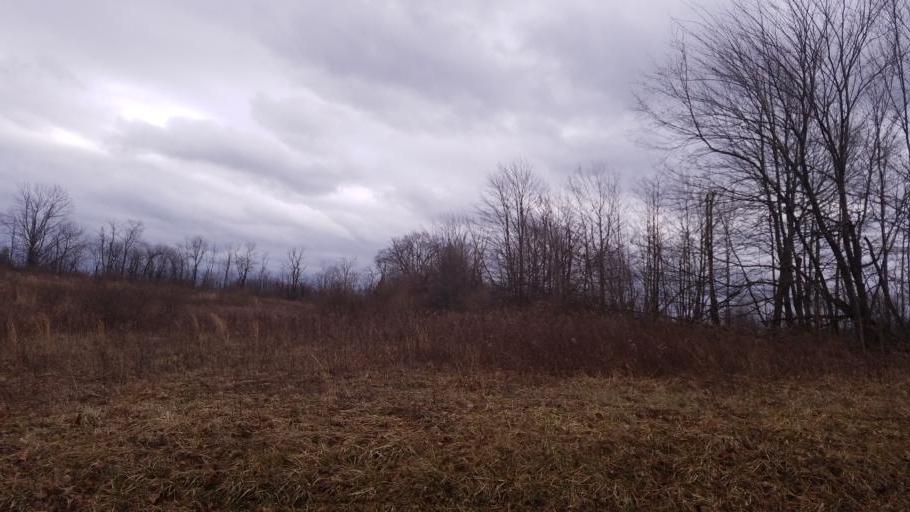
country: US
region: Ohio
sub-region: Knox County
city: Centerburg
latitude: 40.3856
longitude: -82.6166
